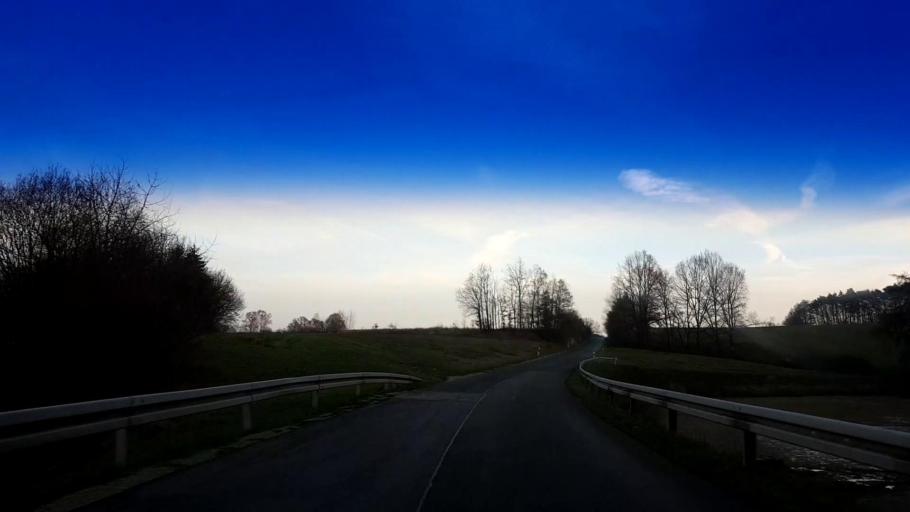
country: DE
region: Bavaria
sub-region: Upper Franconia
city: Stegaurach
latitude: 49.8659
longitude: 10.8169
